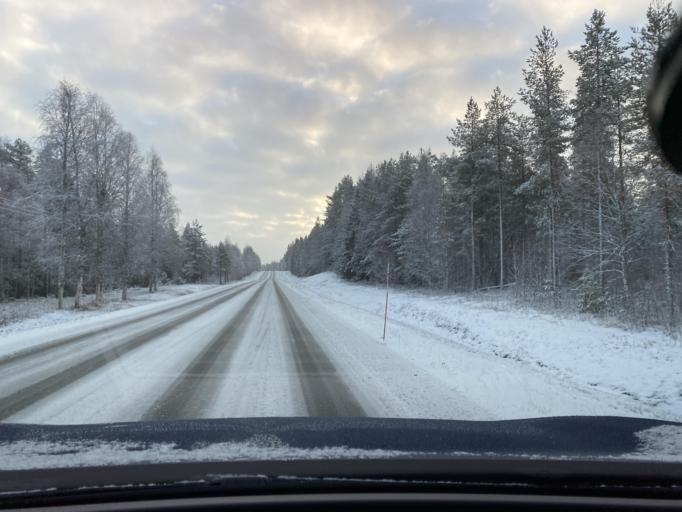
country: FI
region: Lapland
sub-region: Rovaniemi
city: Ranua
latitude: 65.9114
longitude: 26.5165
